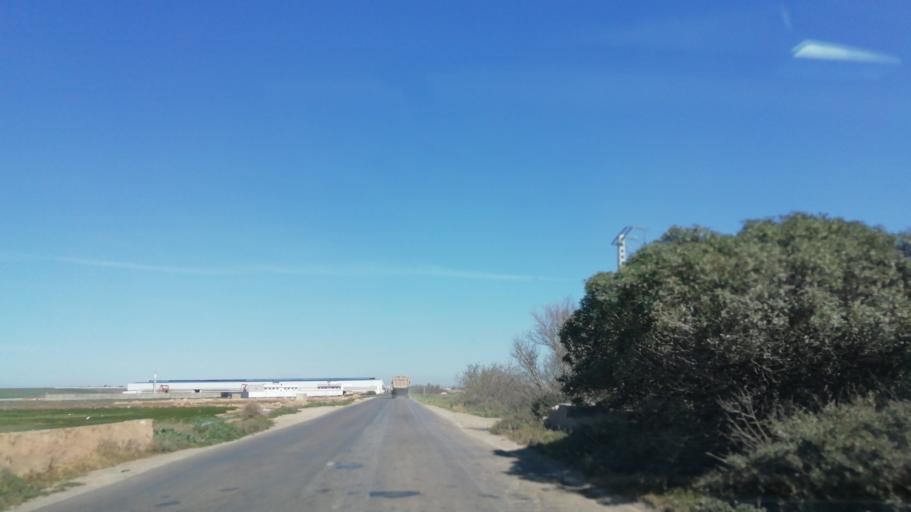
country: DZ
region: Oran
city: Es Senia
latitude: 35.5047
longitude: -0.5935
